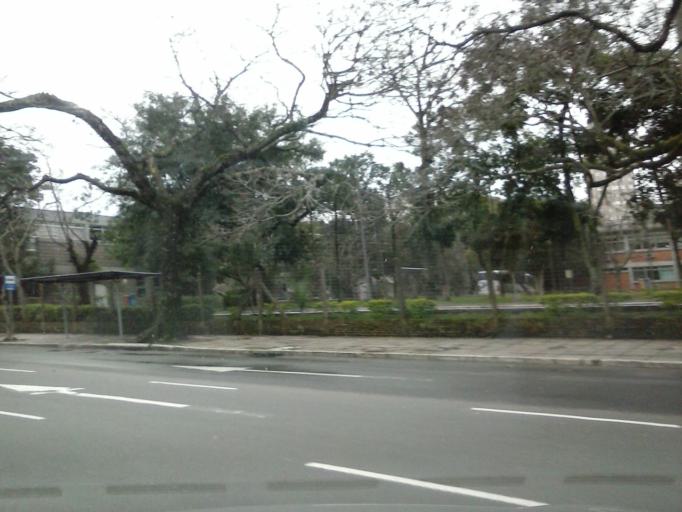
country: BR
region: Rio Grande do Sul
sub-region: Porto Alegre
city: Porto Alegre
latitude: -30.0370
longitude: -51.2356
